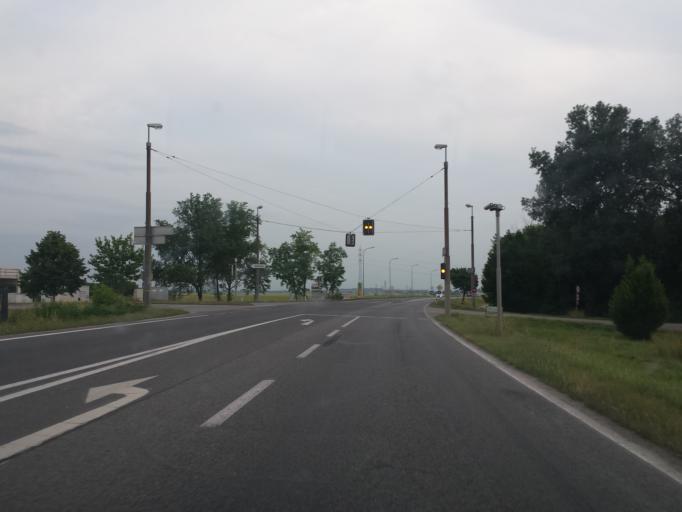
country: AT
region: Lower Austria
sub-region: Politischer Bezirk Ganserndorf
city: Aderklaa
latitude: 48.2841
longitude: 16.5292
